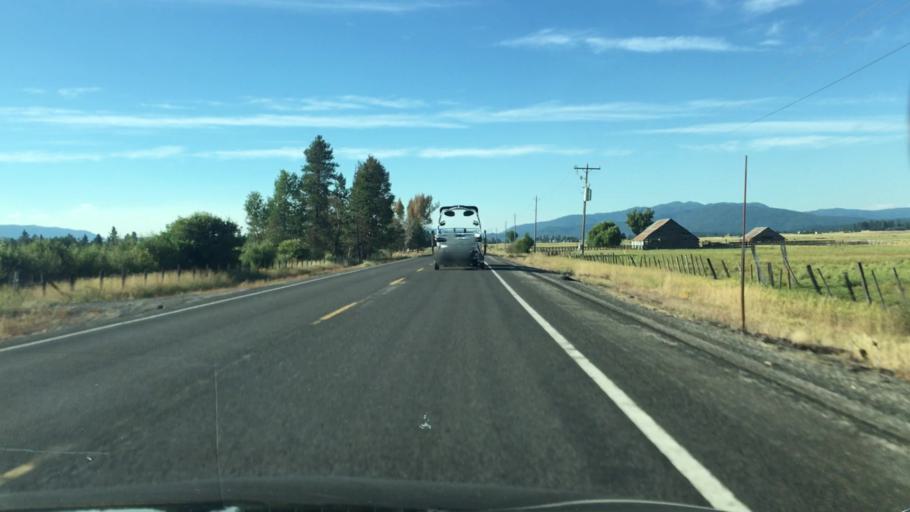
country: US
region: Idaho
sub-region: Valley County
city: Cascade
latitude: 44.4294
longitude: -115.9995
